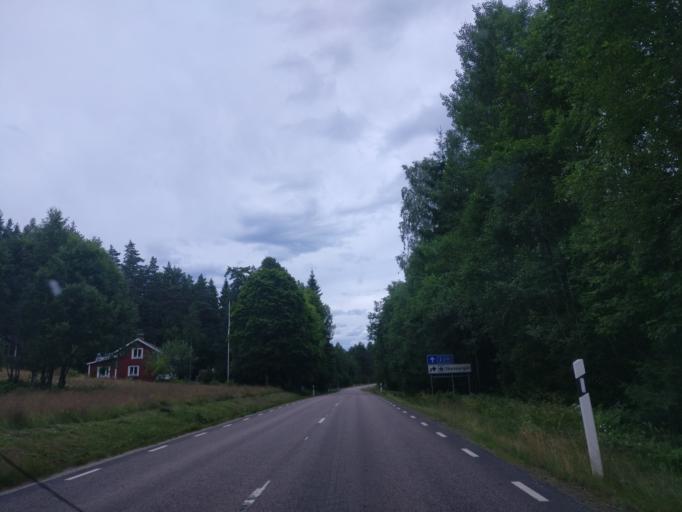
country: SE
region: Vaermland
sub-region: Hagfors Kommun
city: Ekshaerad
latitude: 60.1659
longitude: 13.4775
